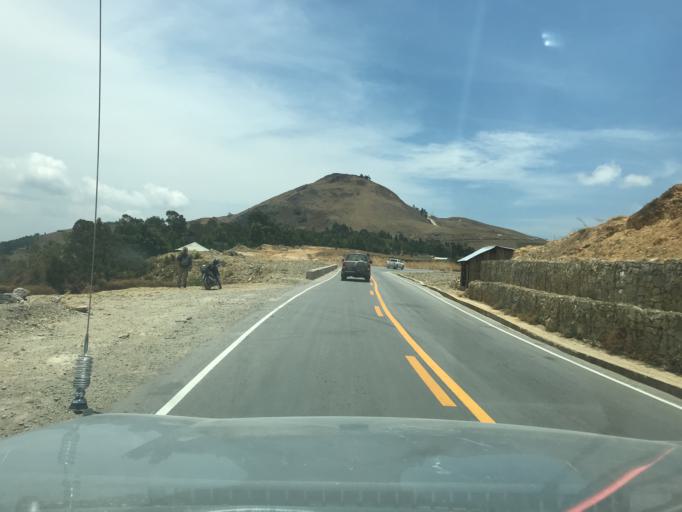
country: TL
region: Manufahi
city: Same
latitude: -8.8776
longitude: 125.5998
